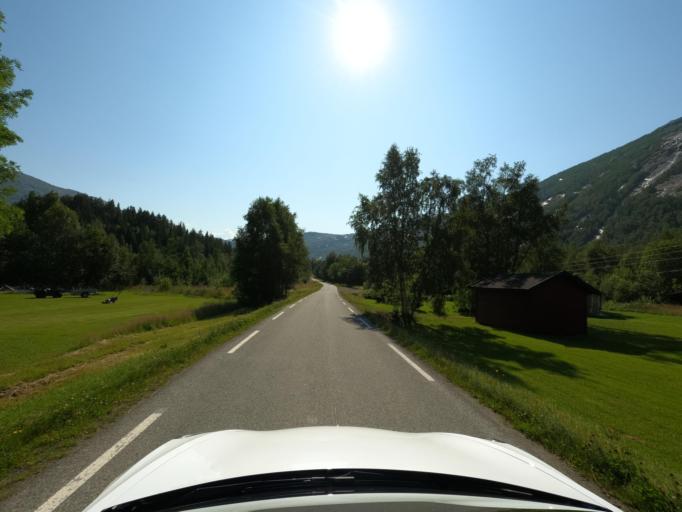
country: NO
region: Nordland
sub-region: Narvik
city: Narvik
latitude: 68.1787
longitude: 17.5524
